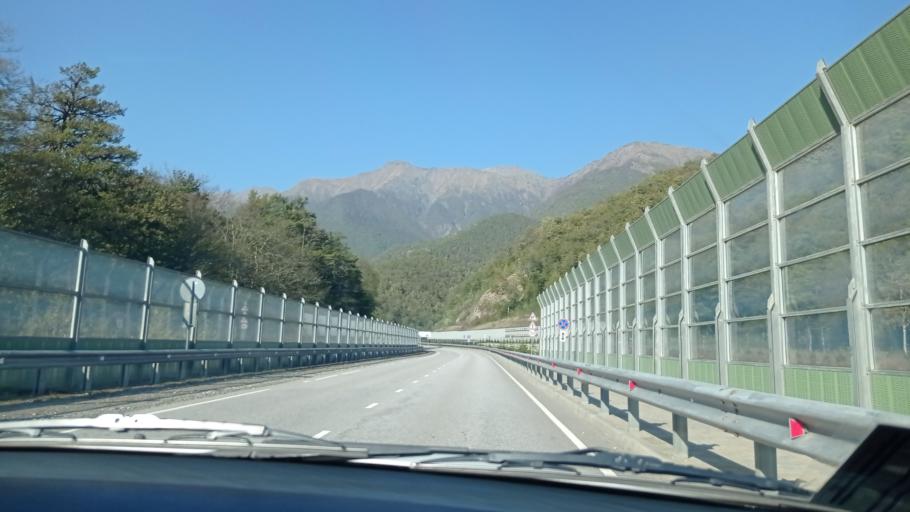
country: RU
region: Krasnodarskiy
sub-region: Sochi City
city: Krasnaya Polyana
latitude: 43.6952
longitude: 40.2692
